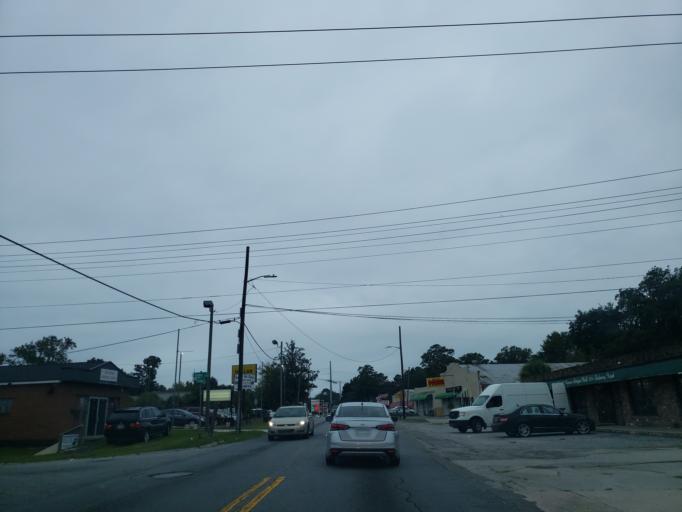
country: US
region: Georgia
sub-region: Chatham County
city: Thunderbolt
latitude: 32.0368
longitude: -81.0666
